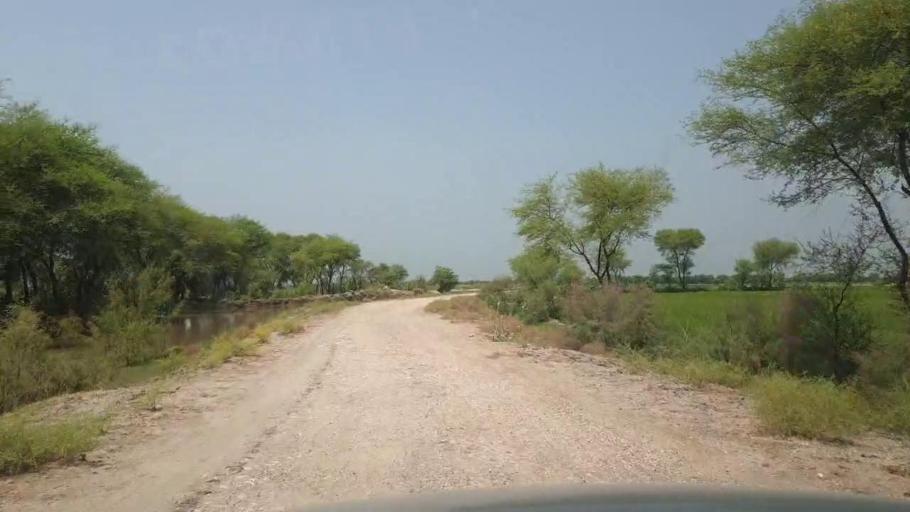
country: PK
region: Sindh
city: Garhi Yasin
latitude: 27.8368
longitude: 68.4927
